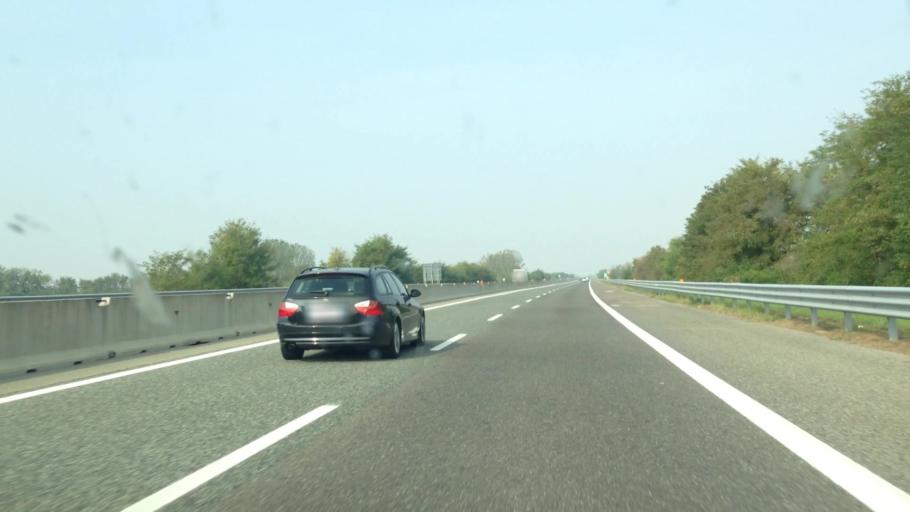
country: IT
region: Piedmont
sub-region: Provincia di Vercelli
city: Asigliano Vercellese
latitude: 45.2582
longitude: 8.4368
